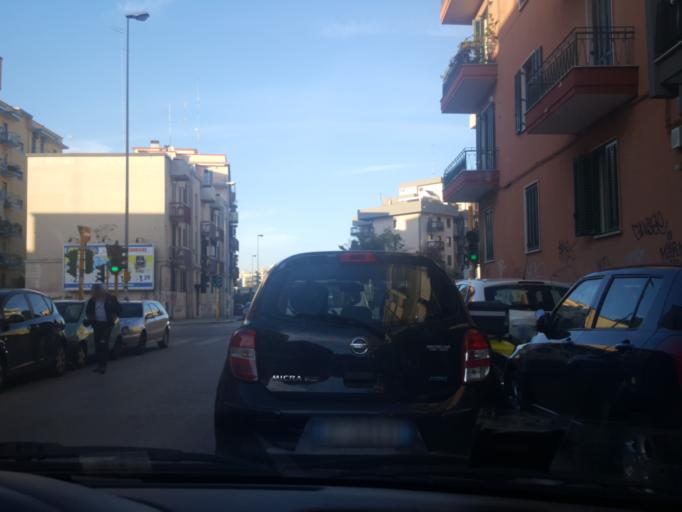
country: IT
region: Apulia
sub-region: Provincia di Bari
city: Bari
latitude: 41.1128
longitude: 16.8686
